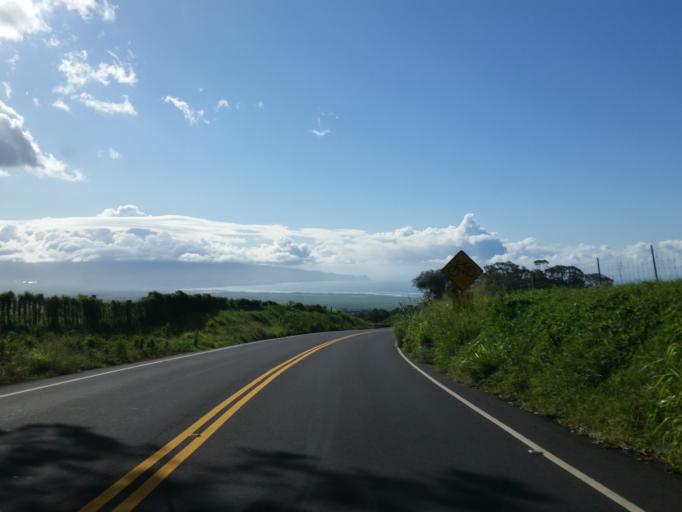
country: US
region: Hawaii
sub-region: Maui County
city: Pukalani
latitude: 20.8221
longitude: -156.3141
